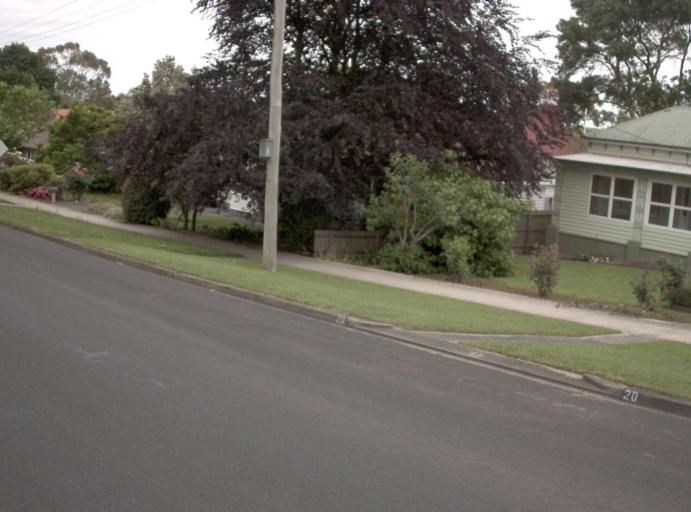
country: AU
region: Victoria
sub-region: Bass Coast
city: North Wonthaggi
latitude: -38.4329
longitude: 145.8221
